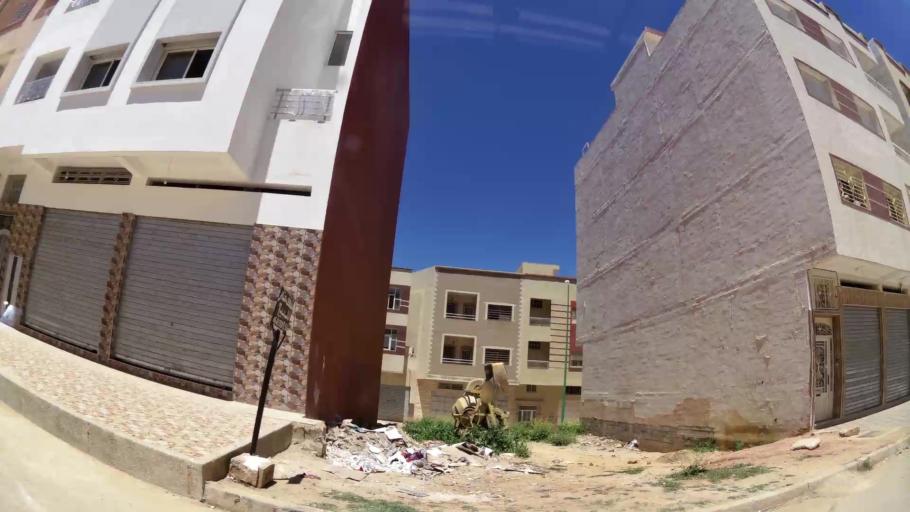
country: MA
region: Meknes-Tafilalet
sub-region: Meknes
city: Meknes
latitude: 33.8571
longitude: -5.5605
